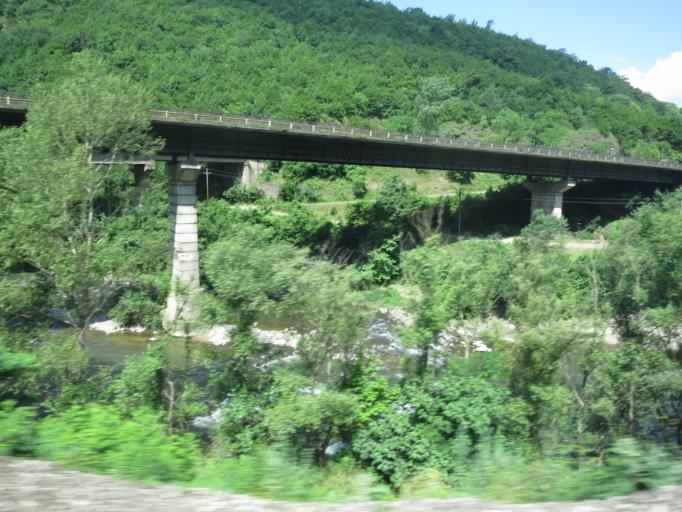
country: GE
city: Shorapani
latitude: 42.0860
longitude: 43.1428
